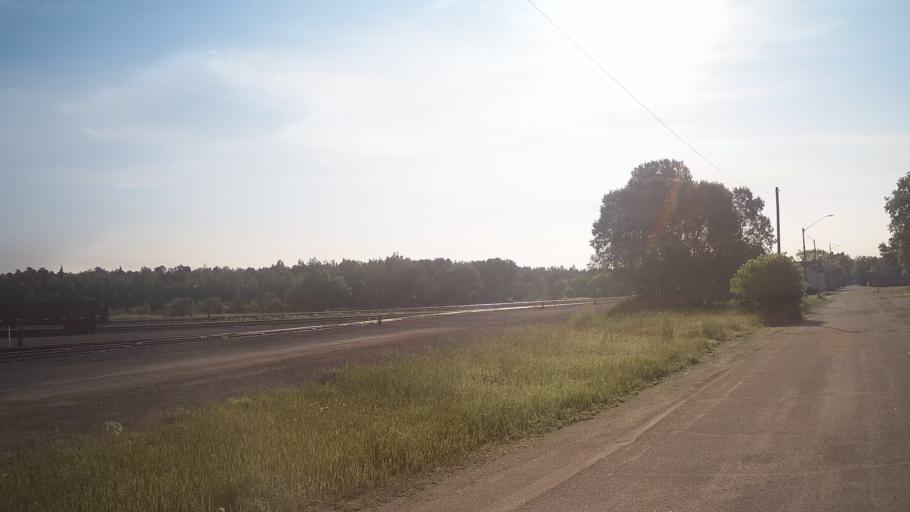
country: CA
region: Ontario
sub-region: Rainy River District
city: Atikokan
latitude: 49.4184
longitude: -91.6646
